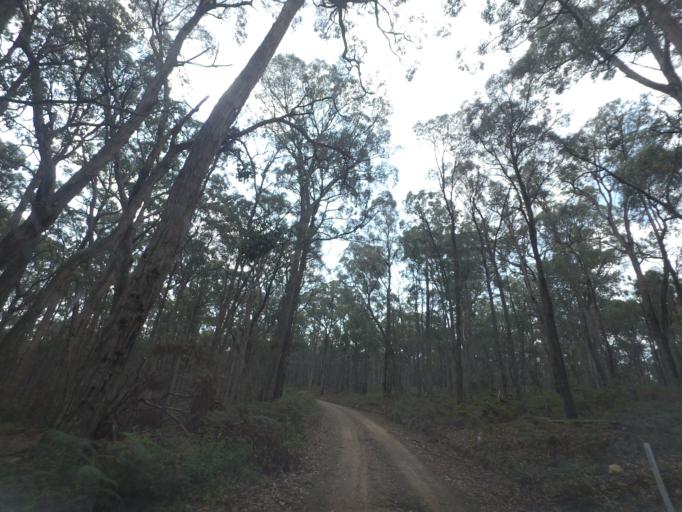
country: AU
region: Victoria
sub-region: Moorabool
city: Bacchus Marsh
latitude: -37.4561
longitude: 144.3565
